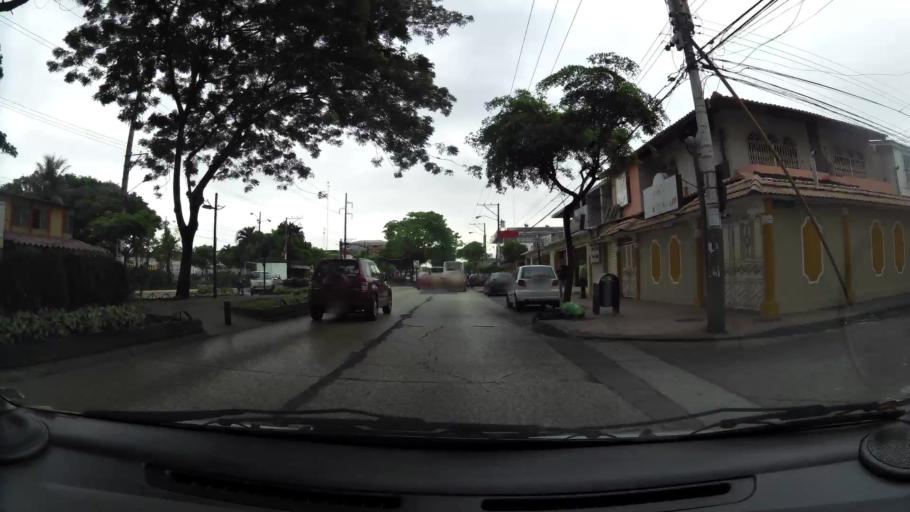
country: EC
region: Guayas
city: Eloy Alfaro
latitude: -2.1362
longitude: -79.9028
